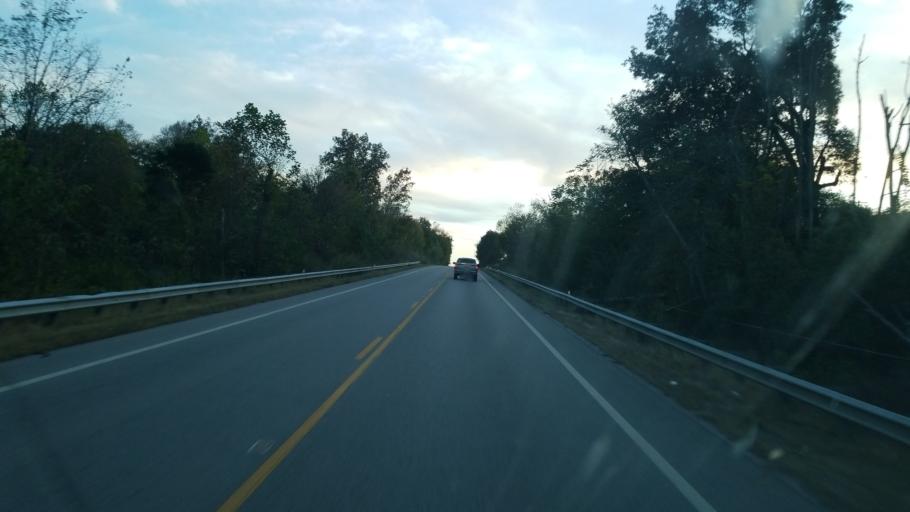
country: US
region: West Virginia
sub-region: Mason County
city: New Haven
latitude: 39.0818
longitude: -81.9273
